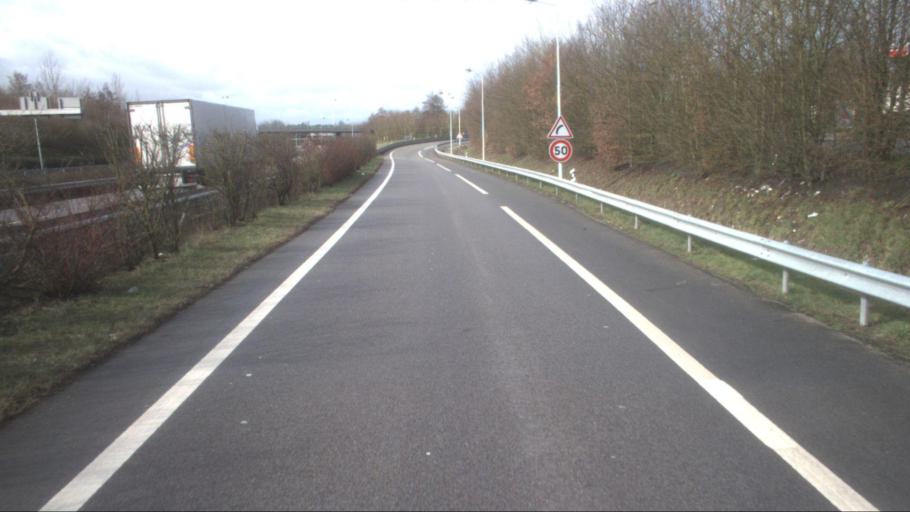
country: FR
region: Ile-de-France
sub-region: Departement des Yvelines
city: Houdan
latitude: 48.7922
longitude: 1.6329
